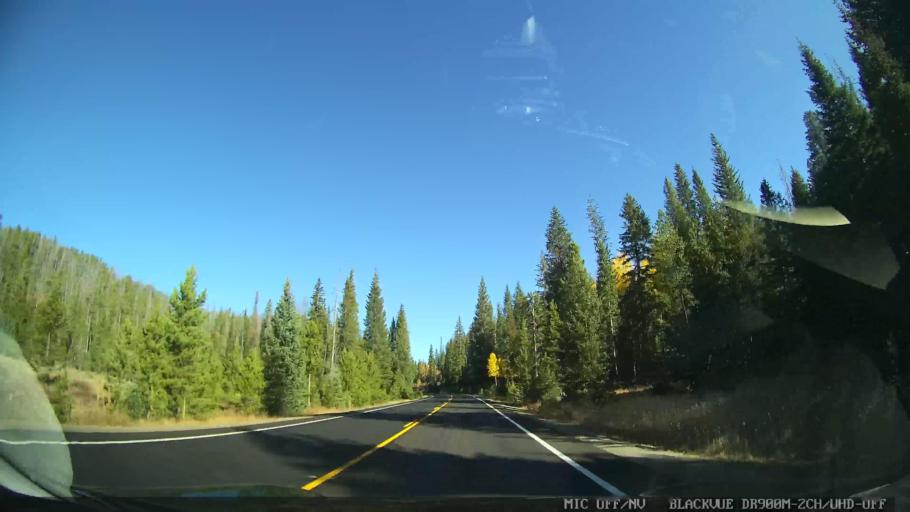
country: US
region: Colorado
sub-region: Grand County
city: Granby
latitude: 40.2971
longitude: -105.8427
